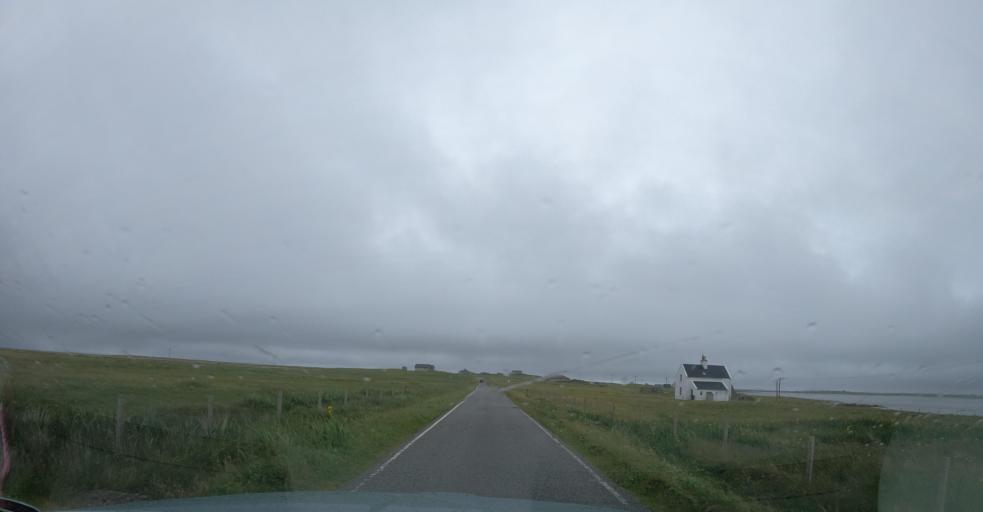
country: GB
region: Scotland
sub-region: Eilean Siar
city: Isle of North Uist
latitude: 57.5587
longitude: -7.3666
